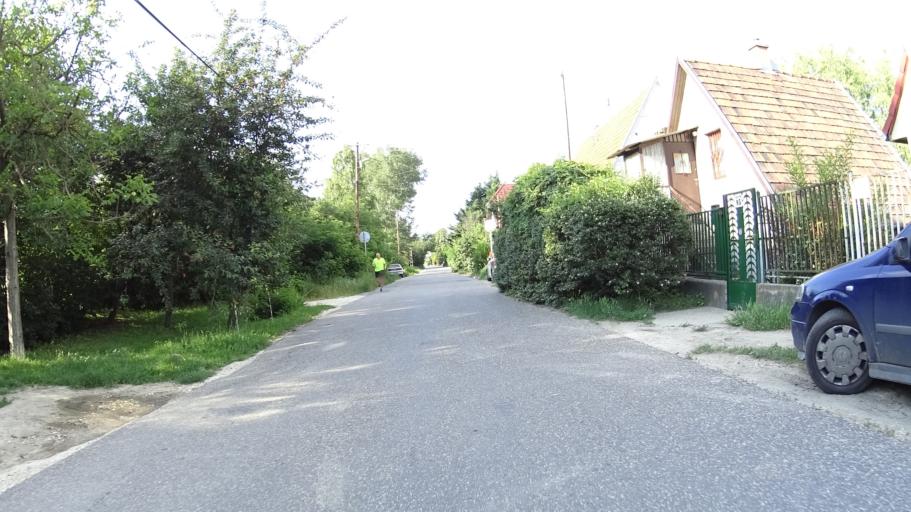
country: HU
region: Pest
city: Dunaharaszti
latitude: 47.3697
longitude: 19.0862
